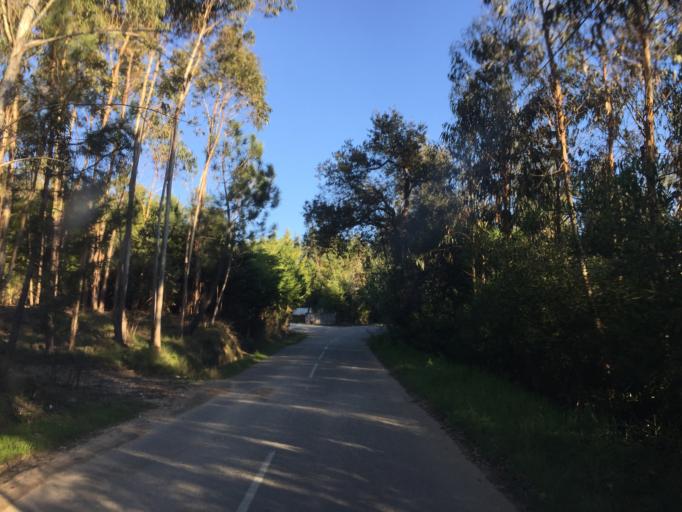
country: PT
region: Coimbra
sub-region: Figueira da Foz
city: Alhadas
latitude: 40.1619
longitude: -8.8055
